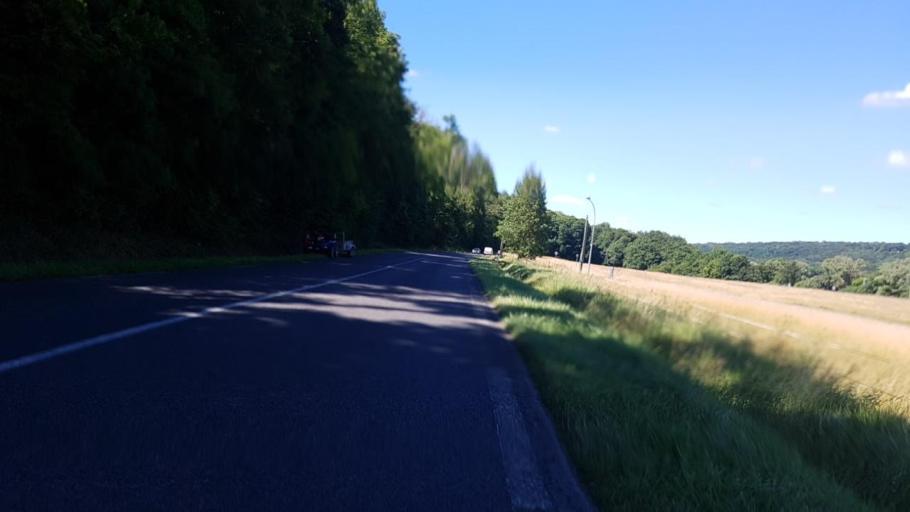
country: FR
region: Ile-de-France
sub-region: Departement de Seine-et-Marne
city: Chamigny
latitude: 48.9672
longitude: 3.1644
